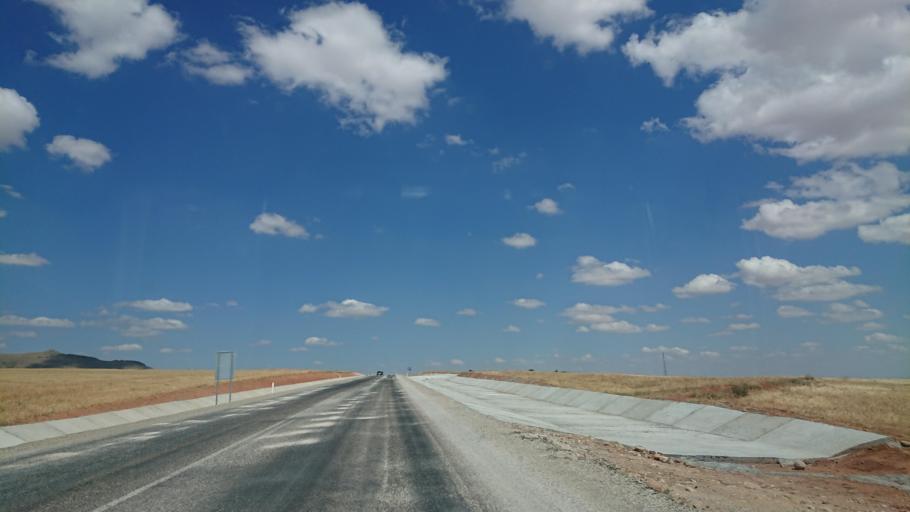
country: TR
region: Kirsehir
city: Kirsehir
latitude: 39.1237
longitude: 33.9745
